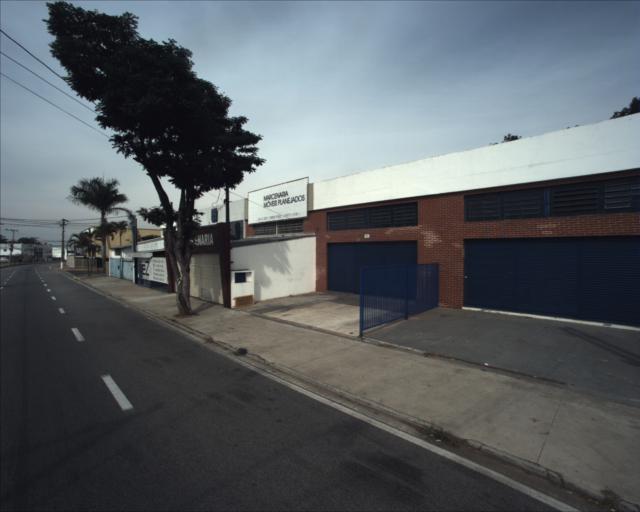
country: BR
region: Sao Paulo
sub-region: Sorocaba
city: Sorocaba
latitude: -23.4647
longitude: -47.4302
